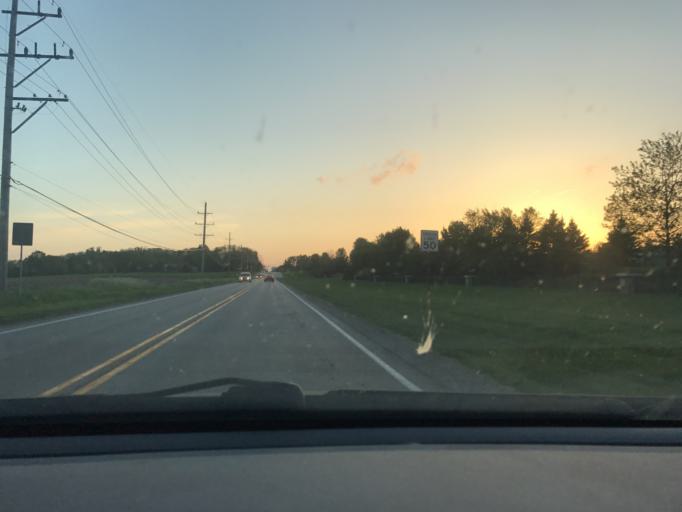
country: US
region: Illinois
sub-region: Kane County
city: South Elgin
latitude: 42.0068
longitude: -88.3531
